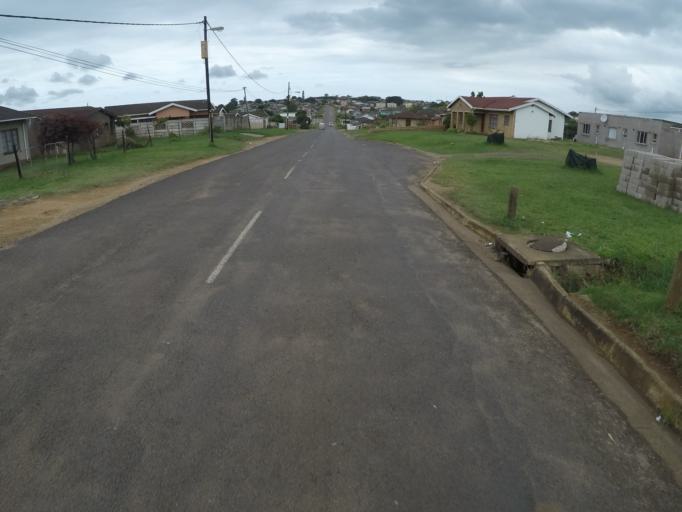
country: ZA
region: KwaZulu-Natal
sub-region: uThungulu District Municipality
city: Empangeni
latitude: -28.7801
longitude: 31.8500
